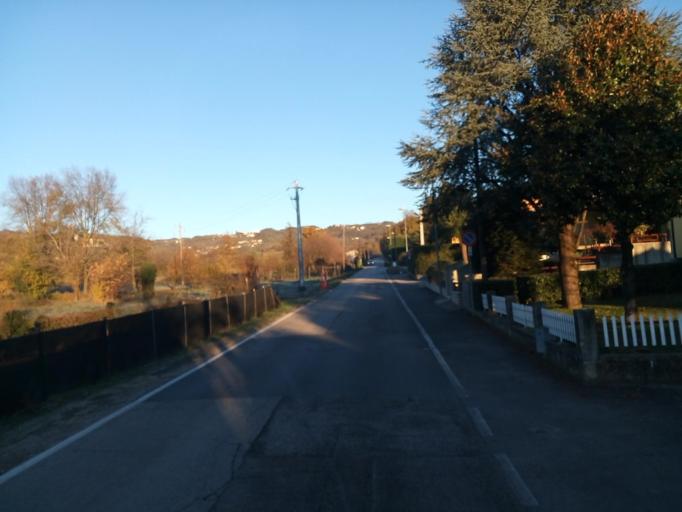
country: IT
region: Veneto
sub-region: Provincia di Vicenza
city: Trissino
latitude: 45.5647
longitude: 11.3614
